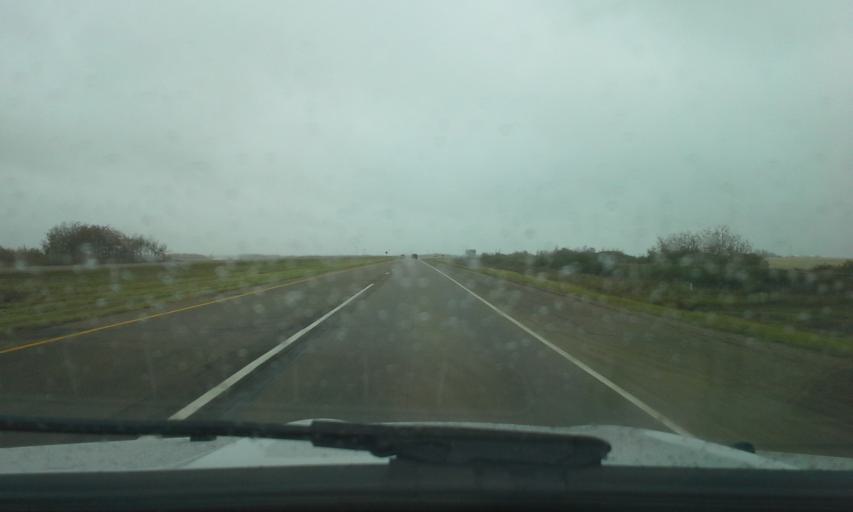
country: CA
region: Saskatchewan
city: Lloydminster
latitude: 53.2295
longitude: -109.8329
